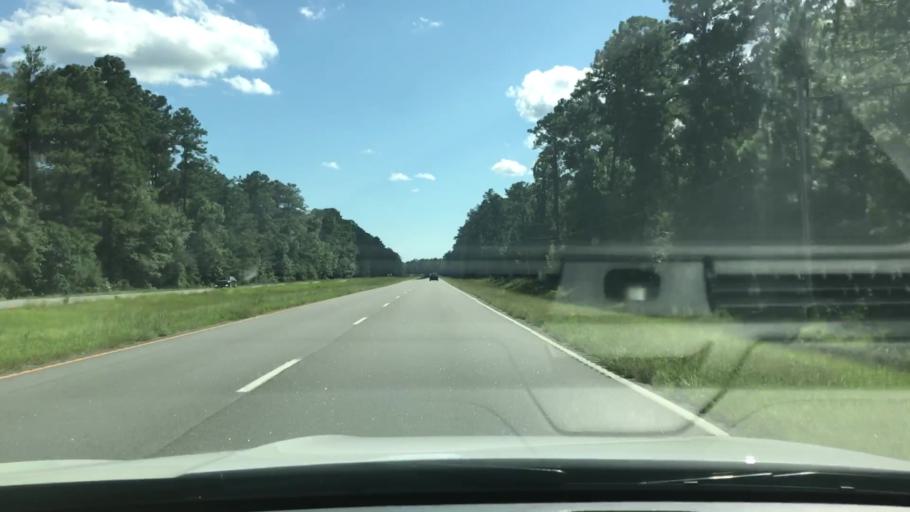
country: US
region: South Carolina
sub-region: Georgetown County
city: Georgetown
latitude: 33.2630
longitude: -79.3654
